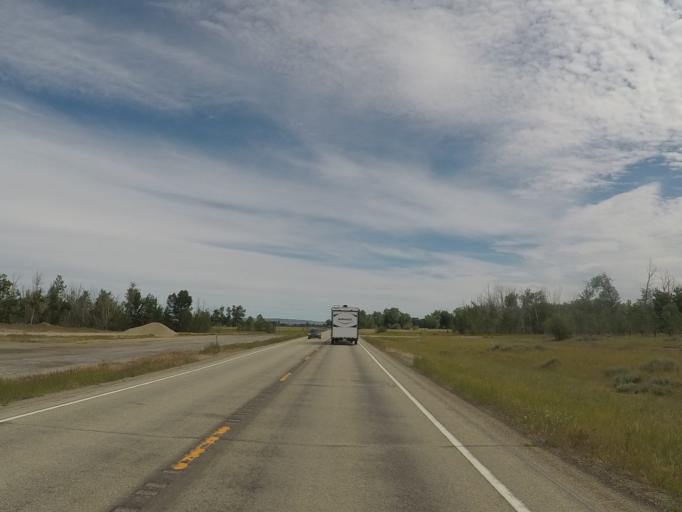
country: US
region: Montana
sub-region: Carbon County
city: Red Lodge
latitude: 45.2872
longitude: -109.2113
